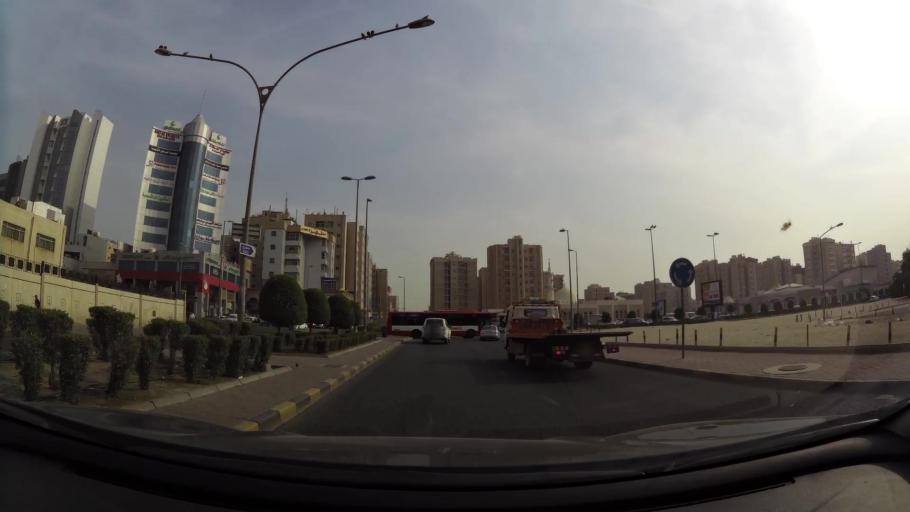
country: KW
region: Al Farwaniyah
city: Al Farwaniyah
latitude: 29.2808
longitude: 47.9571
